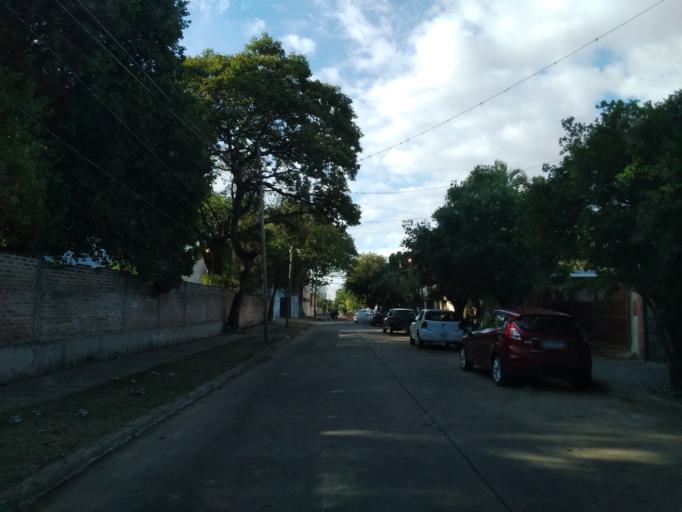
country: AR
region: Corrientes
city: Corrientes
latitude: -27.4602
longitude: -58.8216
